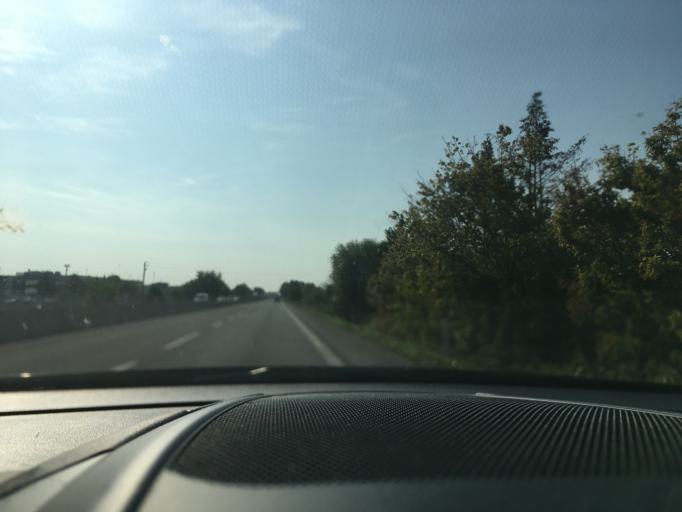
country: IT
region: Emilia-Romagna
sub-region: Provincia di Rimini
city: Bellaria-Igea Marina
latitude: 44.1328
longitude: 12.4649
